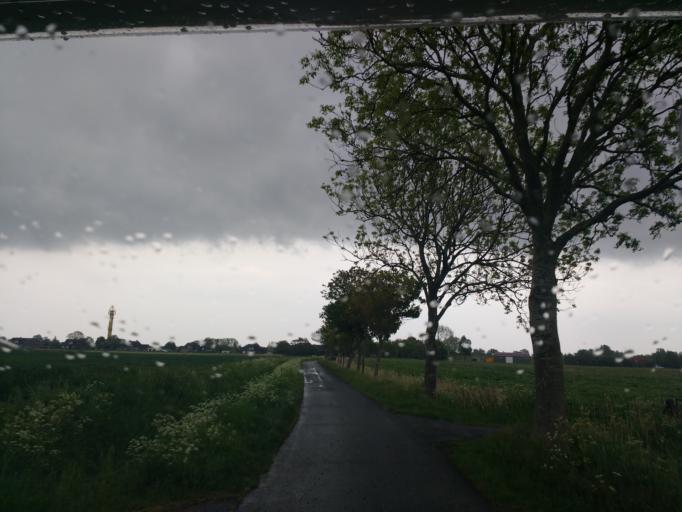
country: DE
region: Lower Saxony
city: Schillig
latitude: 53.7007
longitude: 8.0134
